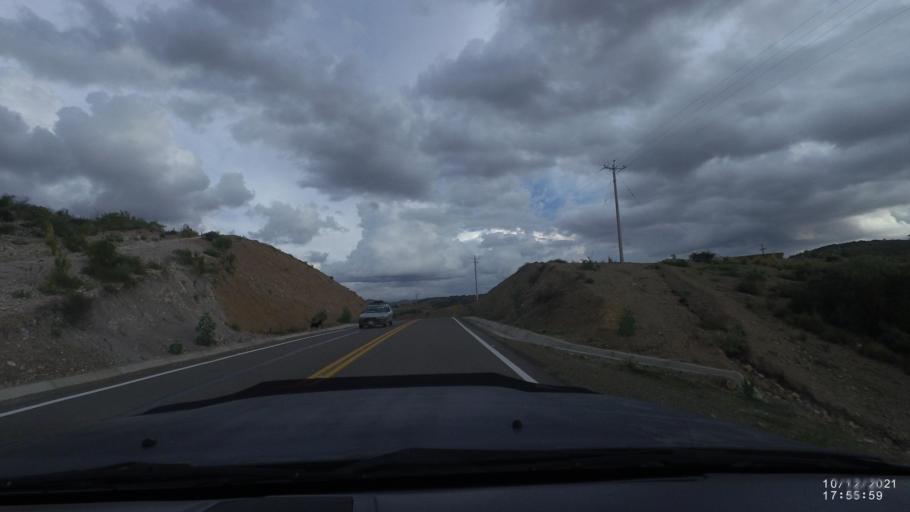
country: BO
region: Cochabamba
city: Cliza
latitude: -17.7137
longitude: -65.9406
